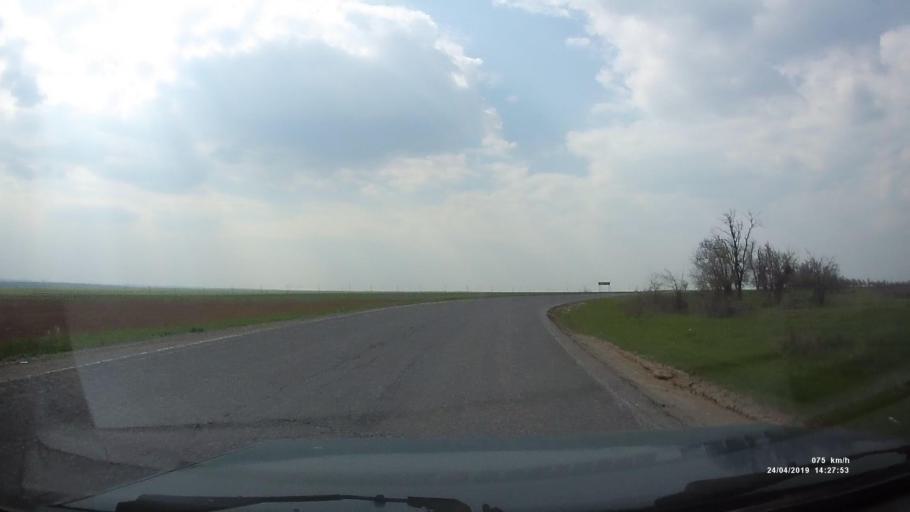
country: RU
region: Kalmykiya
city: Arshan'
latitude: 46.3342
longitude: 44.0356
